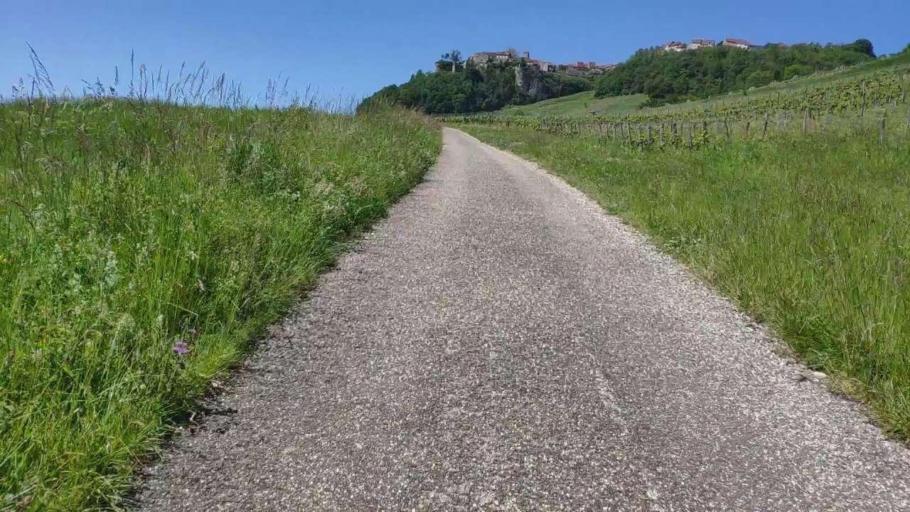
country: FR
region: Franche-Comte
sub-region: Departement du Jura
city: Perrigny
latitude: 46.7466
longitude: 5.6281
